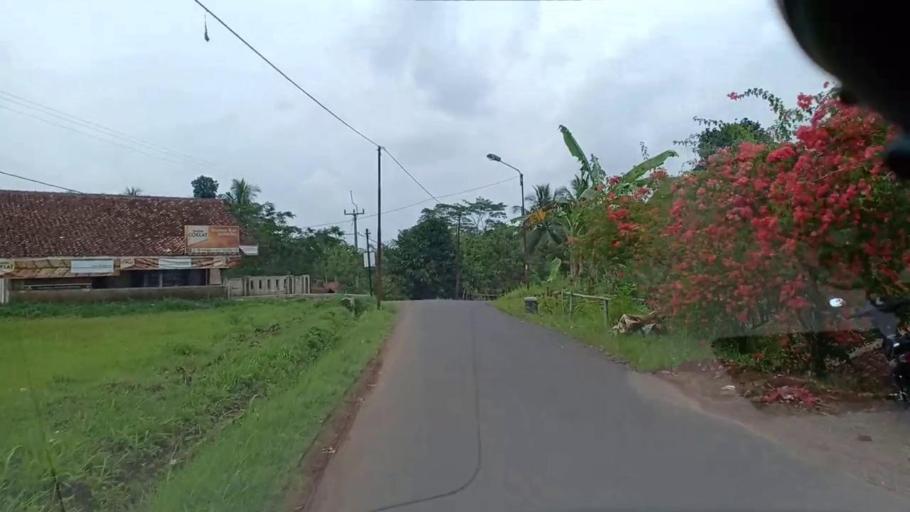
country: ID
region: West Java
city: Kertasari
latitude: -7.3377
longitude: 108.2788
